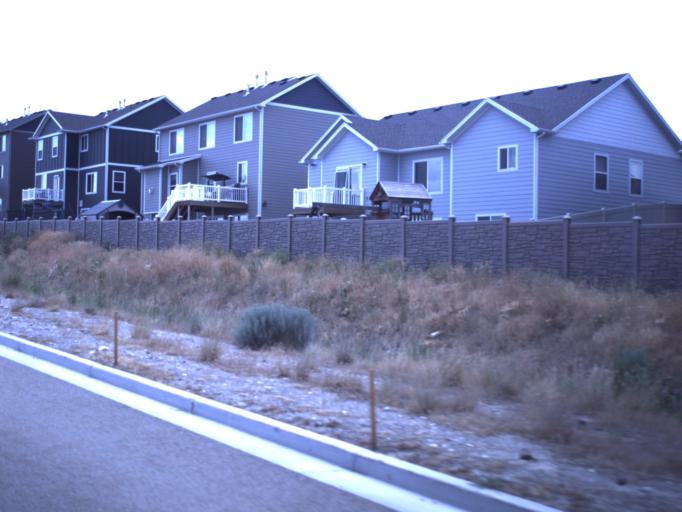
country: US
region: Utah
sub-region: Salt Lake County
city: Herriman
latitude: 40.4900
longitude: -112.0019
